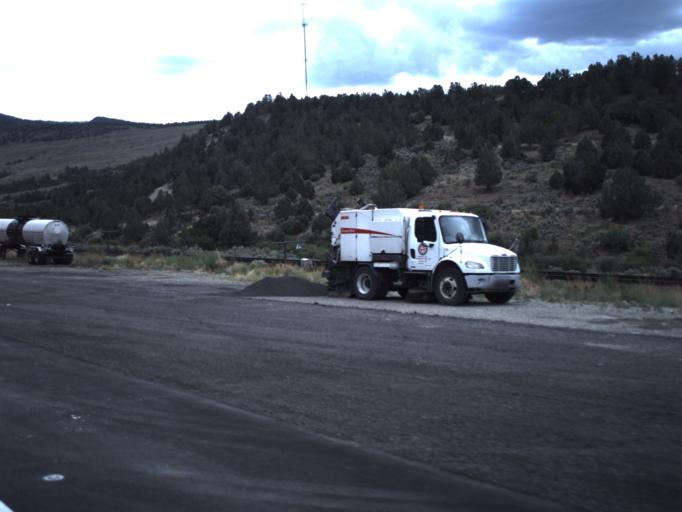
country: US
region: Utah
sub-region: Utah County
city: Mapleton
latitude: 39.9633
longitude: -111.3066
